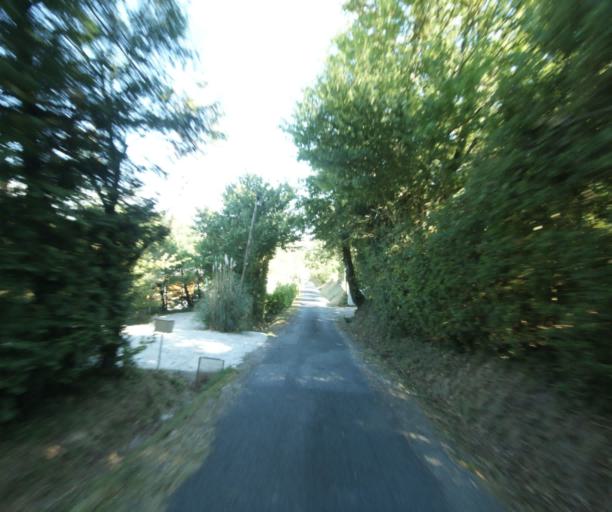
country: FR
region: Midi-Pyrenees
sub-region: Departement de la Haute-Garonne
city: Saint-Felix-Lauragais
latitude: 43.5098
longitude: 1.9390
